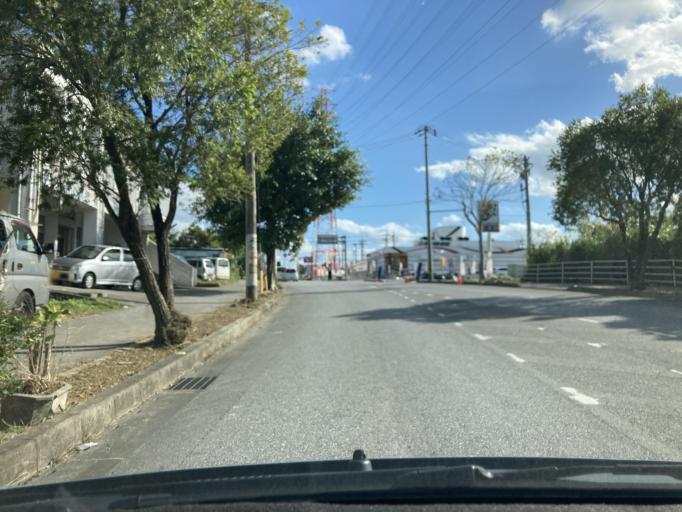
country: JP
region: Okinawa
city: Gushikawa
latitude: 26.3619
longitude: 127.8437
